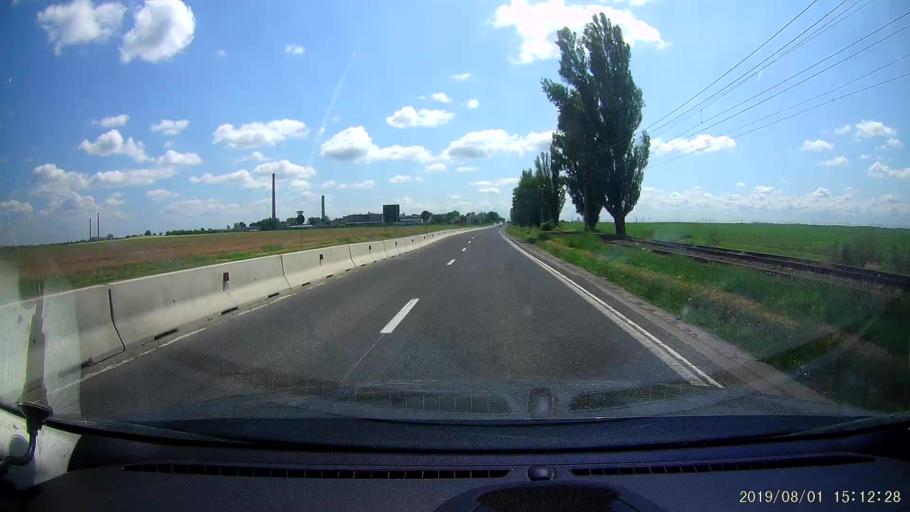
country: RO
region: Braila
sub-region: Comuna Chiscani
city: Lacu Sarat
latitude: 45.2060
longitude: 27.9132
